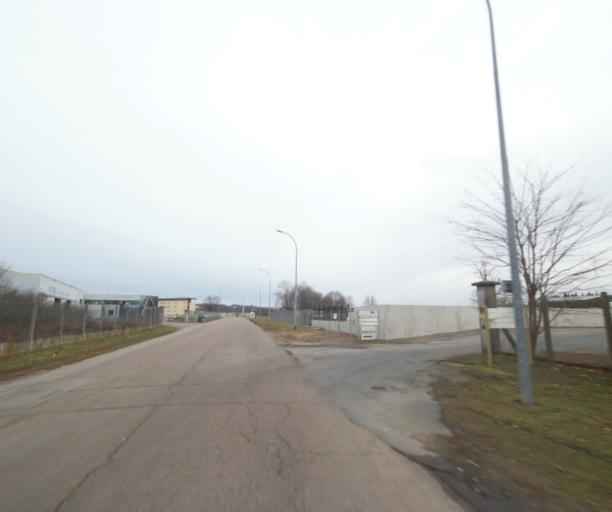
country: FR
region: Rhone-Alpes
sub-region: Departement de la Loire
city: Perreux
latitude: 46.0551
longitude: 4.0974
